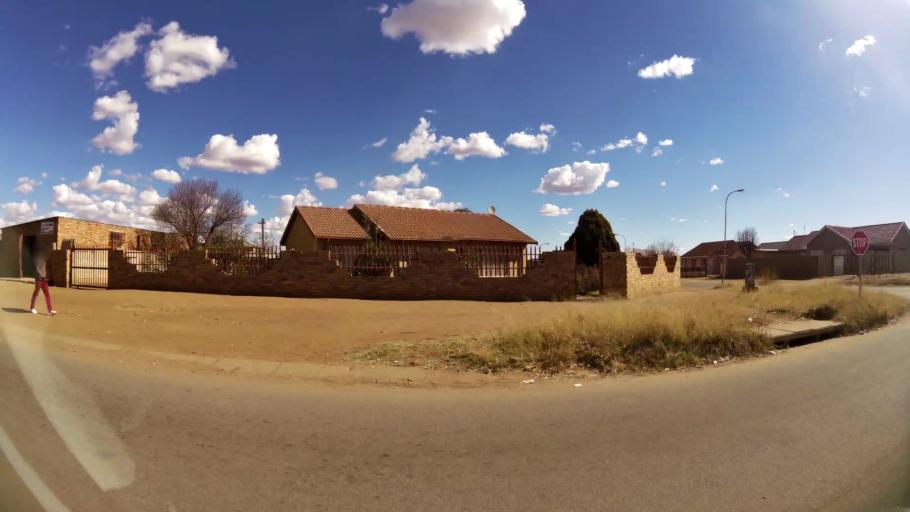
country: ZA
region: North-West
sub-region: Dr Kenneth Kaunda District Municipality
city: Klerksdorp
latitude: -26.8721
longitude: 26.5859
